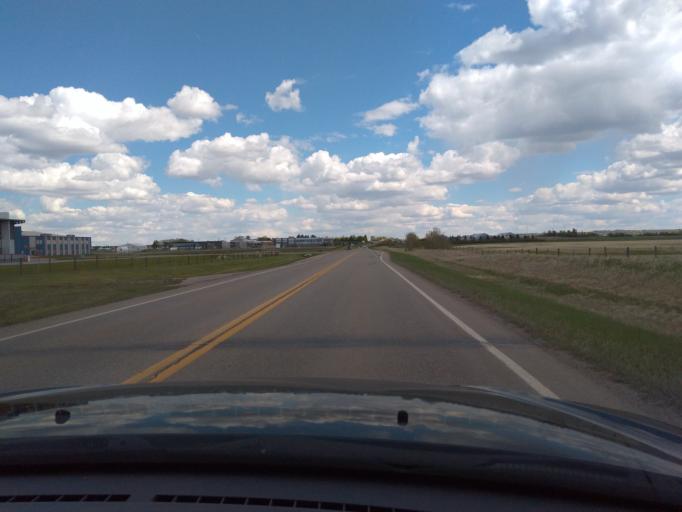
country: CA
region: Alberta
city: Cochrane
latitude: 51.0961
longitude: -114.3699
